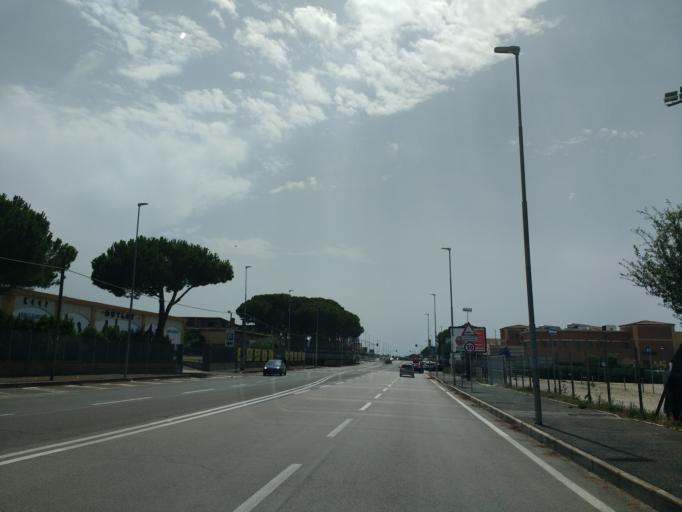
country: IT
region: Latium
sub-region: Citta metropolitana di Roma Capitale
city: Colle del Pino
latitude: 41.7184
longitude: 12.4478
